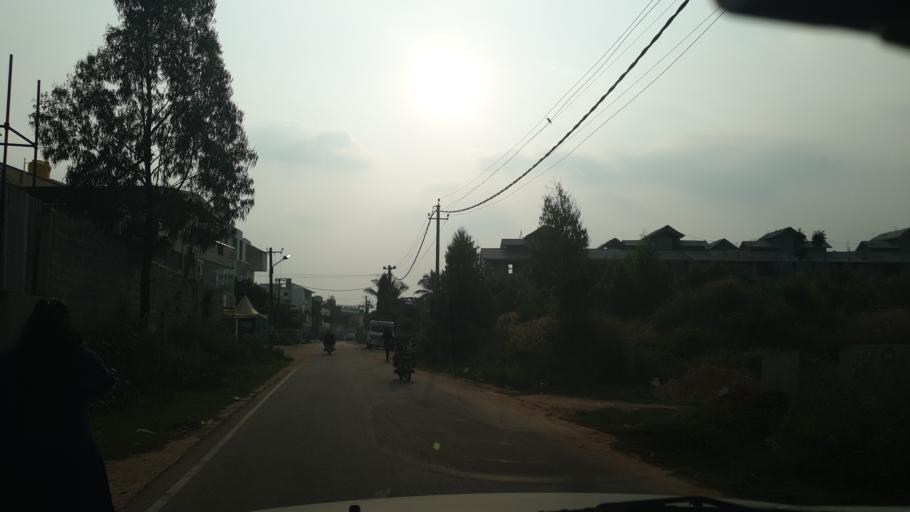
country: IN
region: Karnataka
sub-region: Bangalore Urban
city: Yelahanka
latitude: 13.0672
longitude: 77.6614
